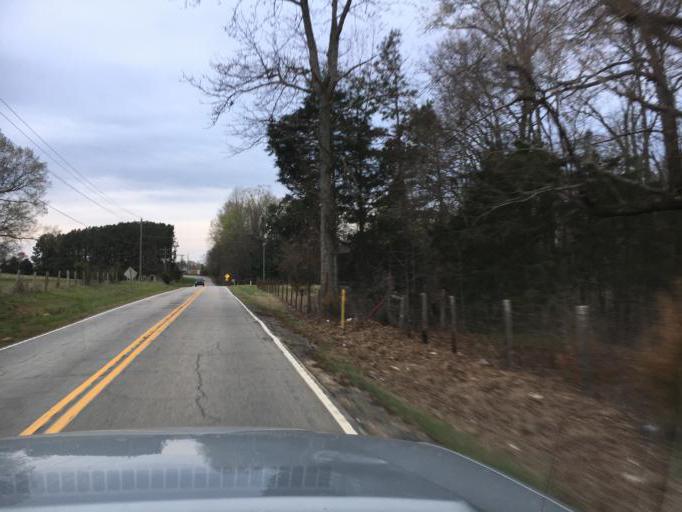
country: US
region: South Carolina
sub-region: Laurens County
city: Laurens
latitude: 34.5384
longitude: -82.0896
